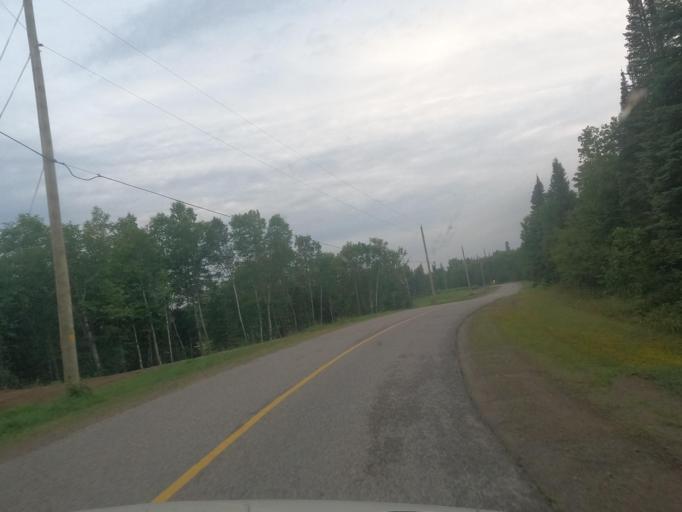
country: CA
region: Ontario
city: Marathon
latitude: 48.7726
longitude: -87.1121
